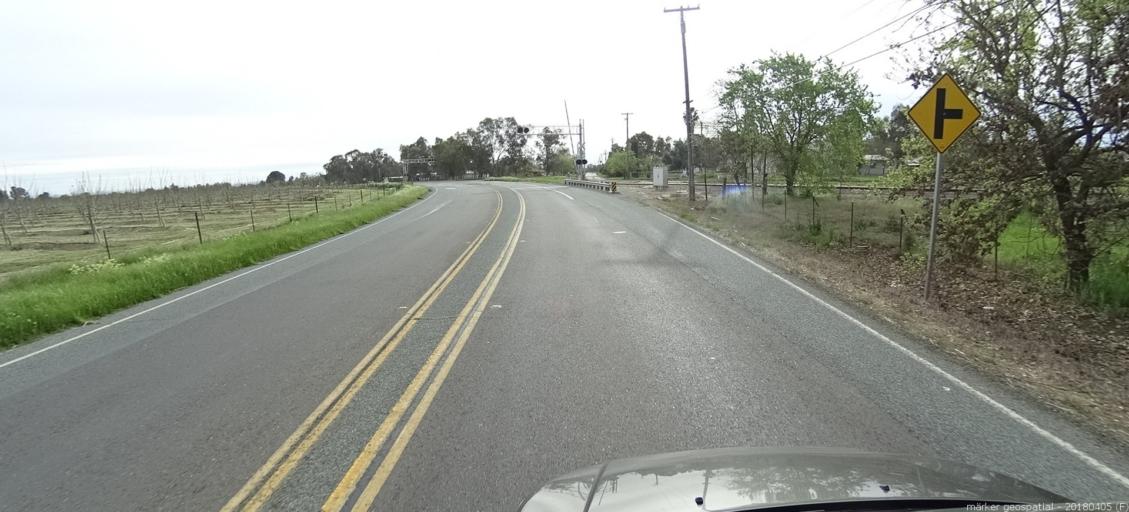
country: US
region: California
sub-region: Sacramento County
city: Herald
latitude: 38.2917
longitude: -121.2530
